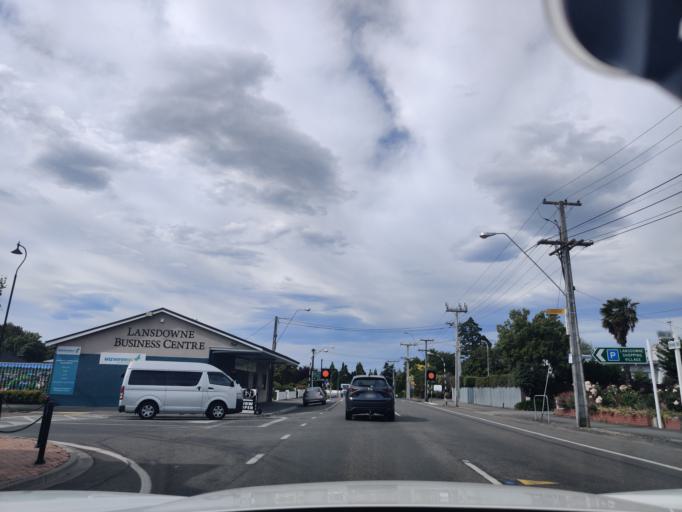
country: NZ
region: Wellington
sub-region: Masterton District
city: Masterton
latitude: -40.9432
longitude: 175.6697
